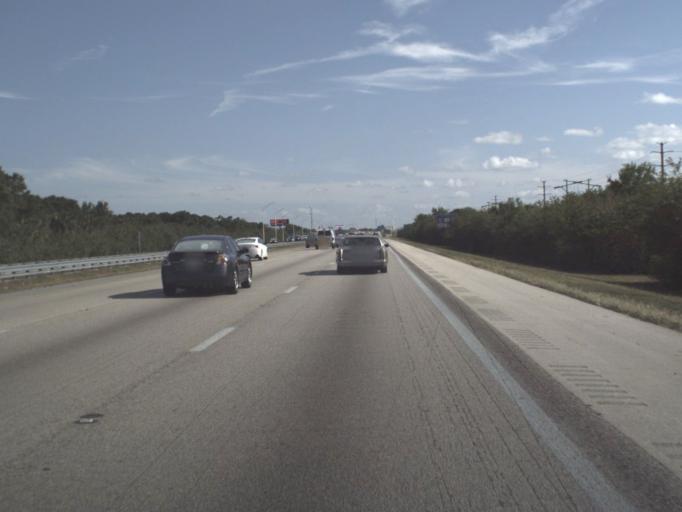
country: US
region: Florida
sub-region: Brevard County
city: June Park
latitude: 28.0940
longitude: -80.7062
